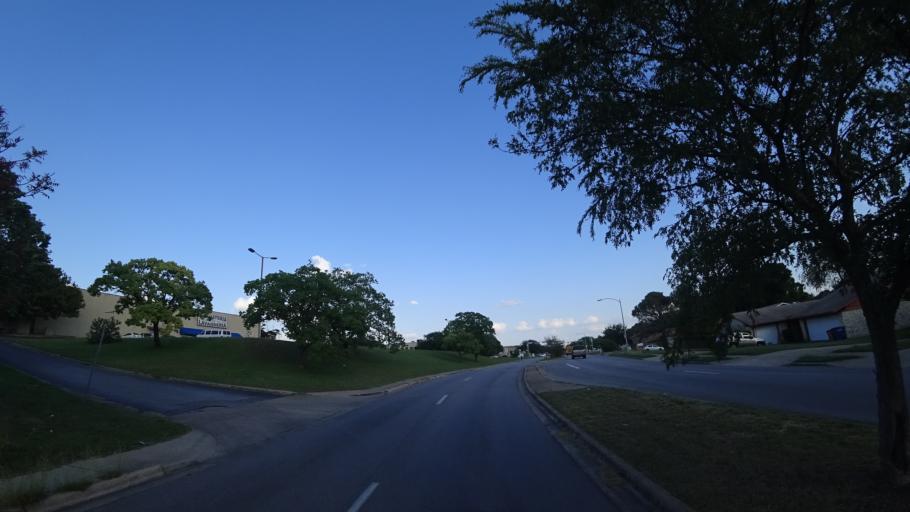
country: US
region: Texas
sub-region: Travis County
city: Wells Branch
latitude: 30.3681
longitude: -97.7077
